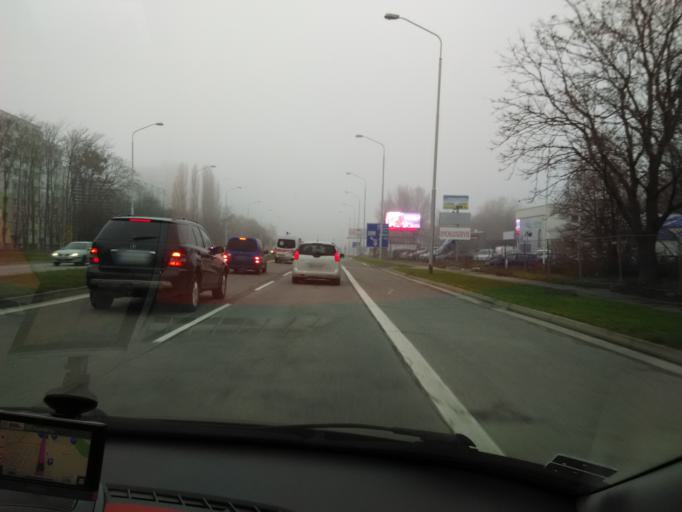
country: SK
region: Bratislavsky
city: Bratislava
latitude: 48.1224
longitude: 17.1339
